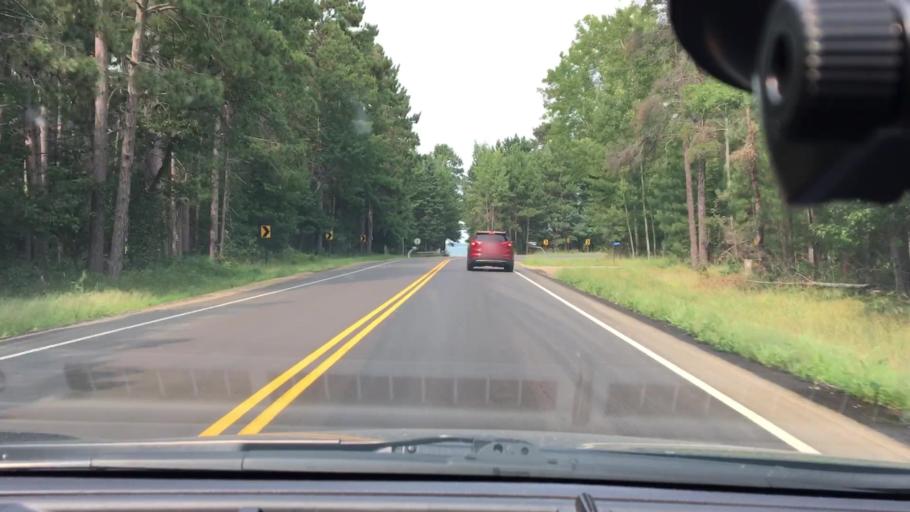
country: US
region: Minnesota
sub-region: Crow Wing County
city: Breezy Point
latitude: 46.5326
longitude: -94.1824
